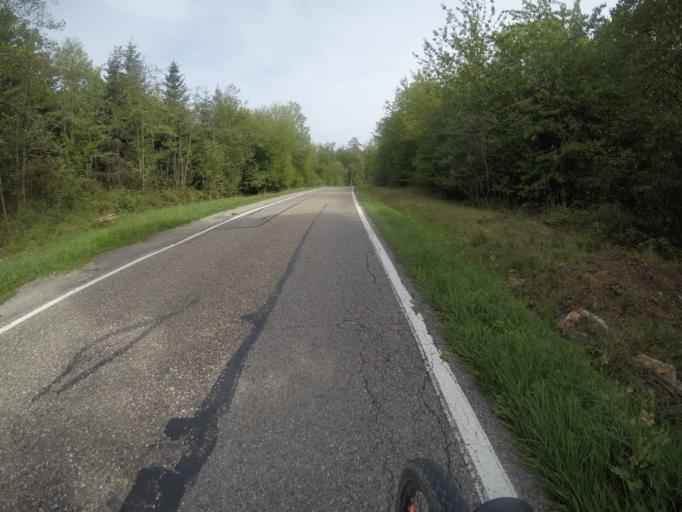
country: DE
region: Baden-Wuerttemberg
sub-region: Karlsruhe Region
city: Eutingen
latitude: 48.8760
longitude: 8.7641
